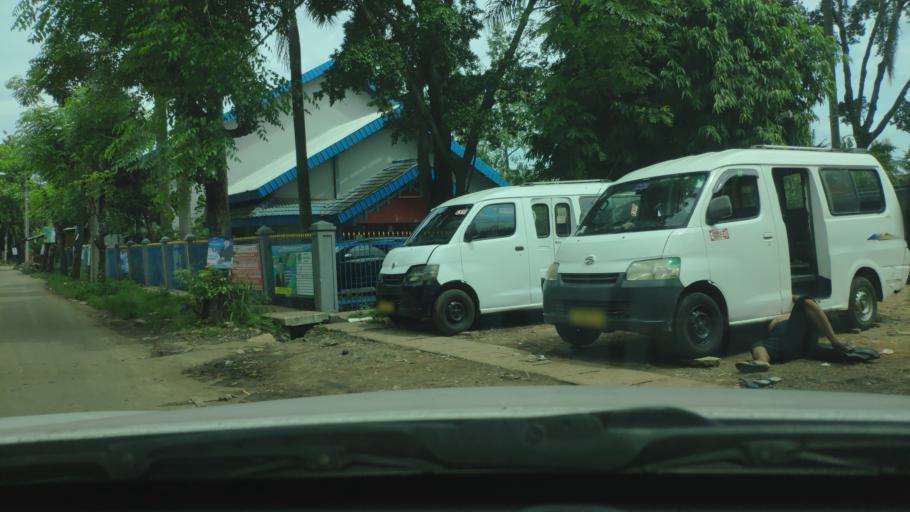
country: ID
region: West Java
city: Ciputat
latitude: -6.2232
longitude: 106.7032
